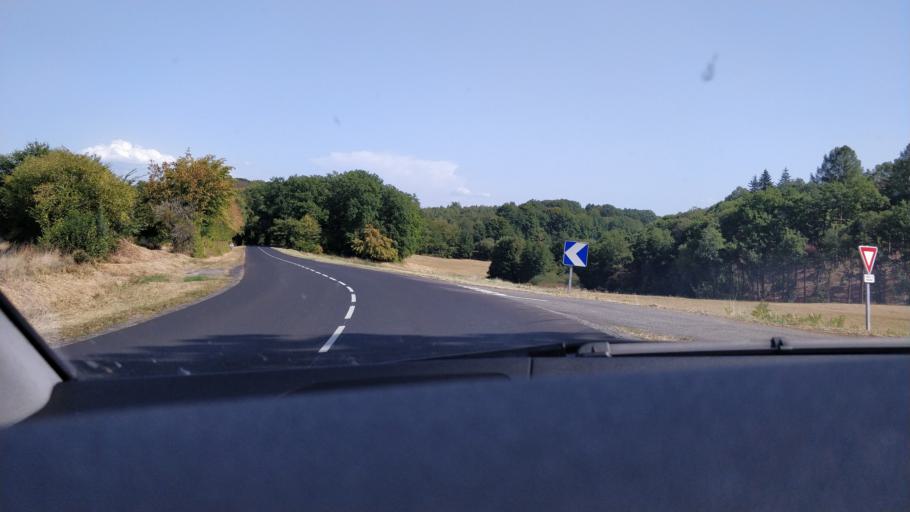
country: FR
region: Limousin
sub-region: Departement de la Correze
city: Uzerche
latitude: 45.4719
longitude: 1.5420
